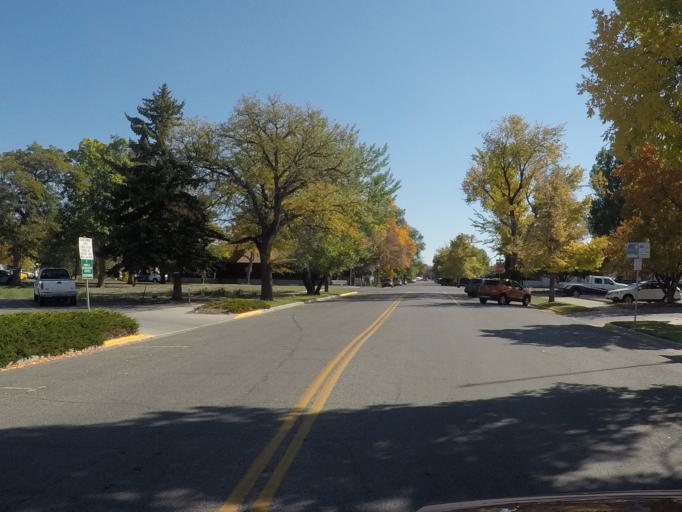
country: US
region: Montana
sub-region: Yellowstone County
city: Billings
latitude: 45.7874
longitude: -108.5019
